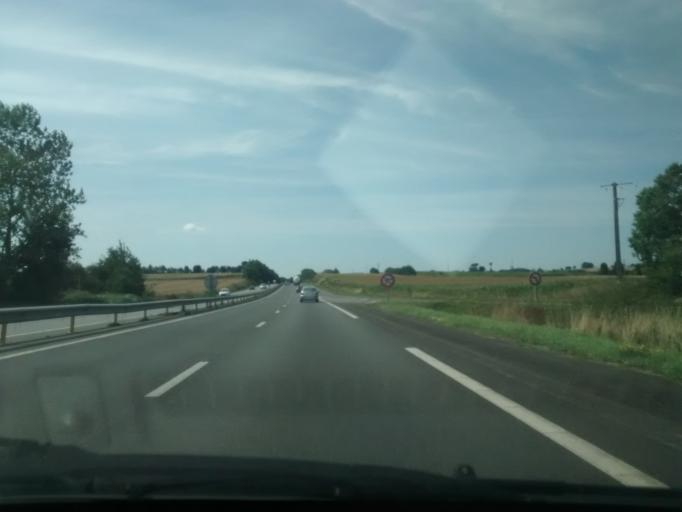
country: FR
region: Brittany
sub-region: Departement des Cotes-d'Armor
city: Plumaugat
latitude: 48.2923
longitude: -2.2157
